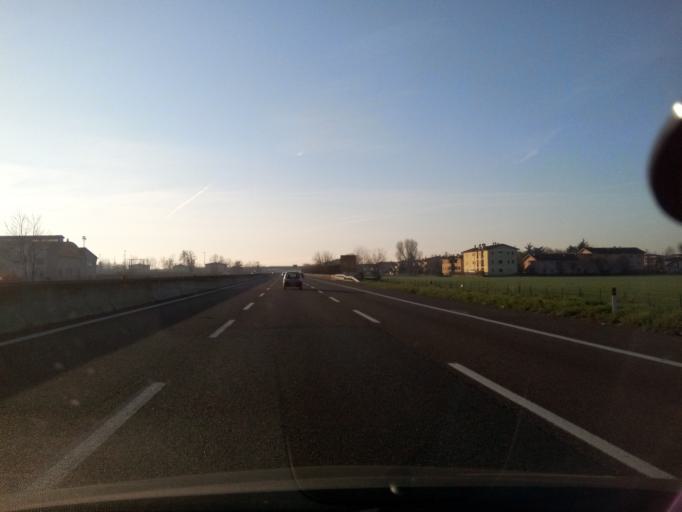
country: IT
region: Lombardy
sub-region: Provincia di Lodi
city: Guardamiglio
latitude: 45.1159
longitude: 9.6792
